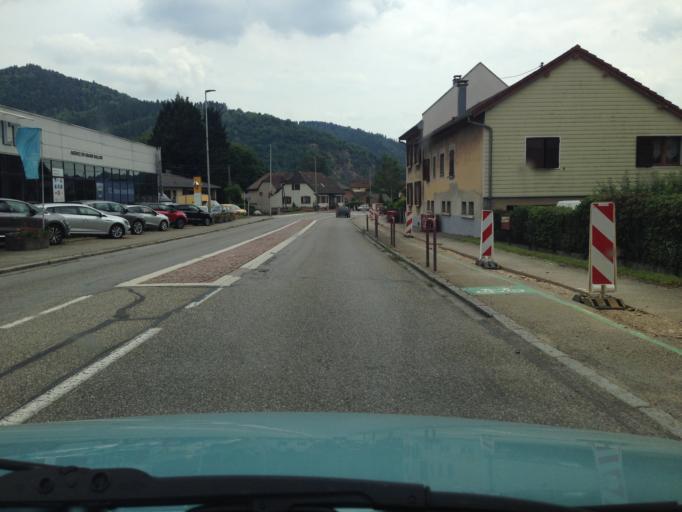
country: FR
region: Alsace
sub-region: Departement du Haut-Rhin
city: Bitschwiller-les-Thann
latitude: 47.8412
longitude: 7.0734
